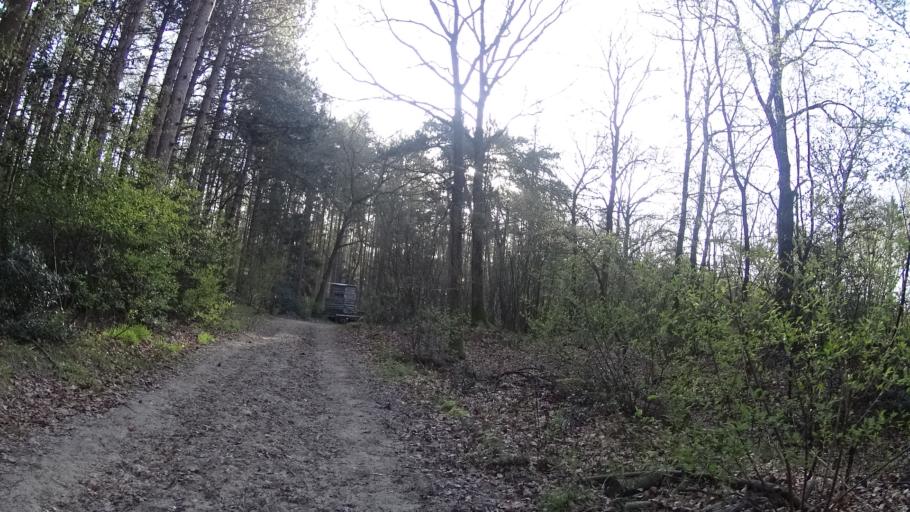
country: DE
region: Lower Saxony
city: Oberlangen
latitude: 52.8155
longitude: 7.2695
